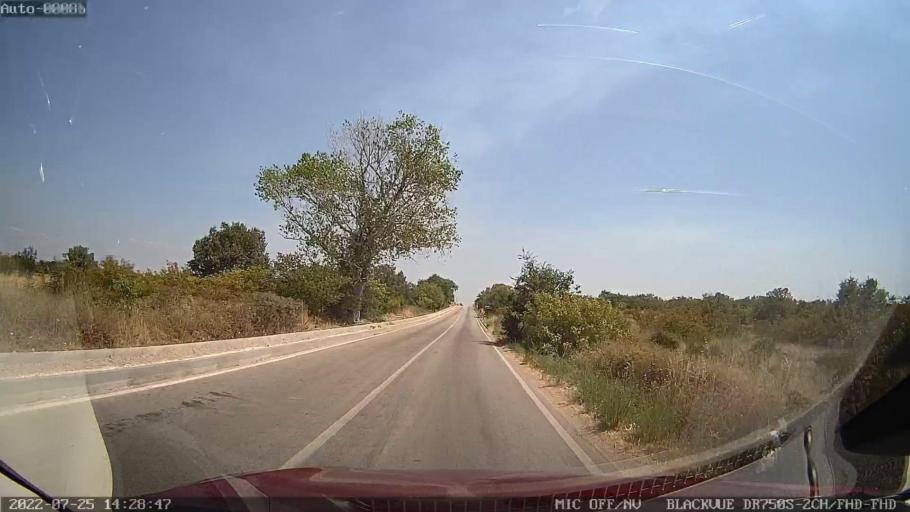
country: HR
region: Zadarska
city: Policnik
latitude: 44.1241
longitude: 15.3500
